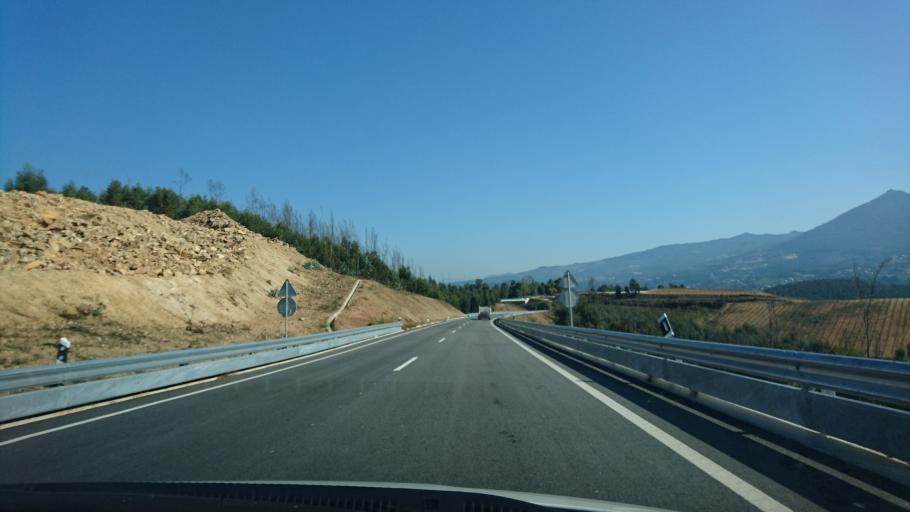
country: PT
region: Braga
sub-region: Celorico de Basto
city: Celorico de Basto
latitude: 41.4008
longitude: -7.9843
